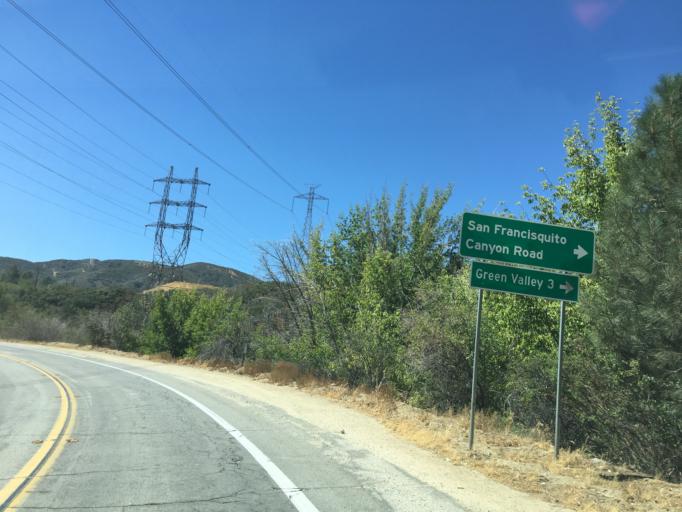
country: US
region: California
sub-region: Los Angeles County
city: Green Valley
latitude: 34.6500
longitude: -118.3773
